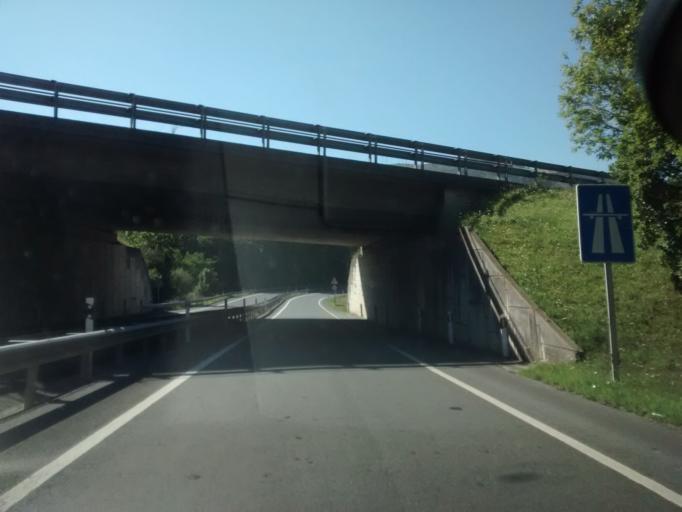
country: ES
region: Basque Country
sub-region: Provincia de Guipuzcoa
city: Cestona
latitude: 43.2656
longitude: -2.2727
